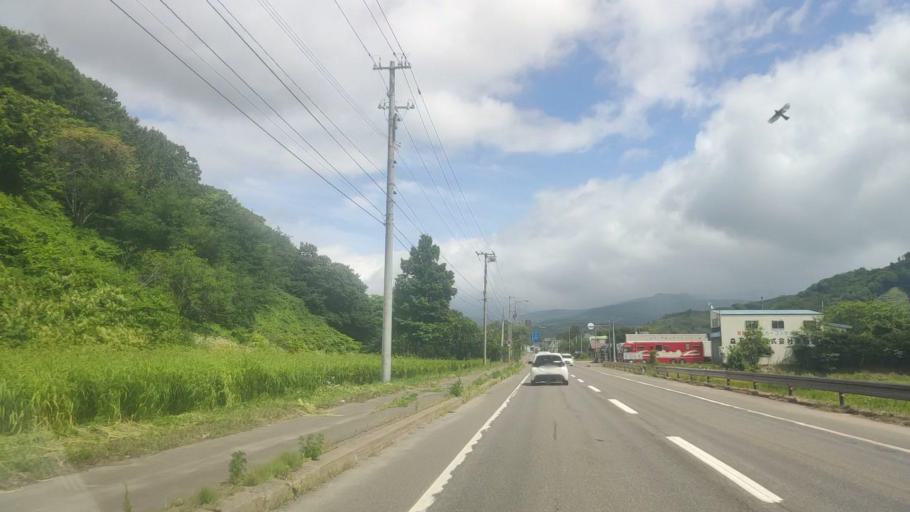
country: JP
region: Hokkaido
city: Date
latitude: 42.5790
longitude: 140.9506
